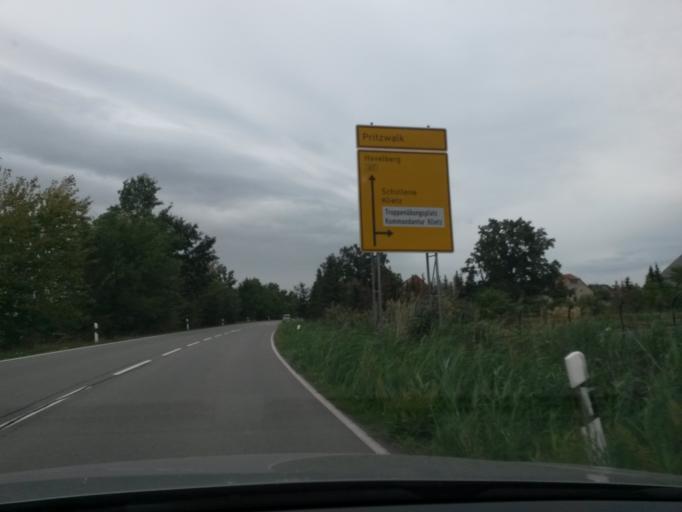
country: DE
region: Saxony-Anhalt
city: Klietz
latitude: 52.6698
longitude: 12.0610
